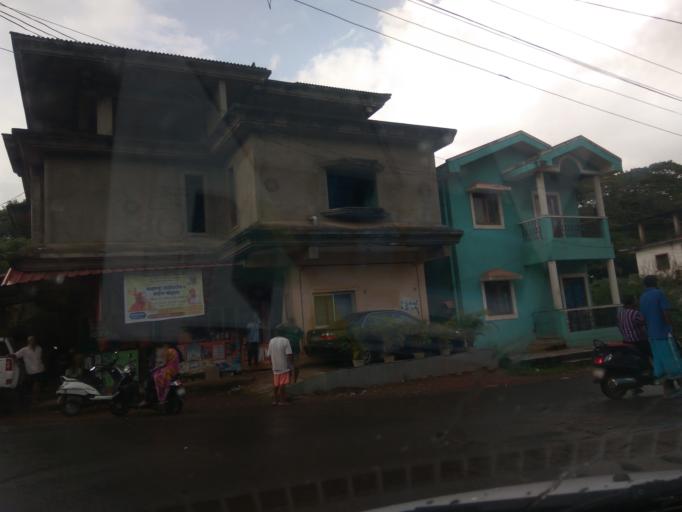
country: IN
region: Goa
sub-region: North Goa
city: Goa Velha
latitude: 15.4432
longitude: 73.8653
